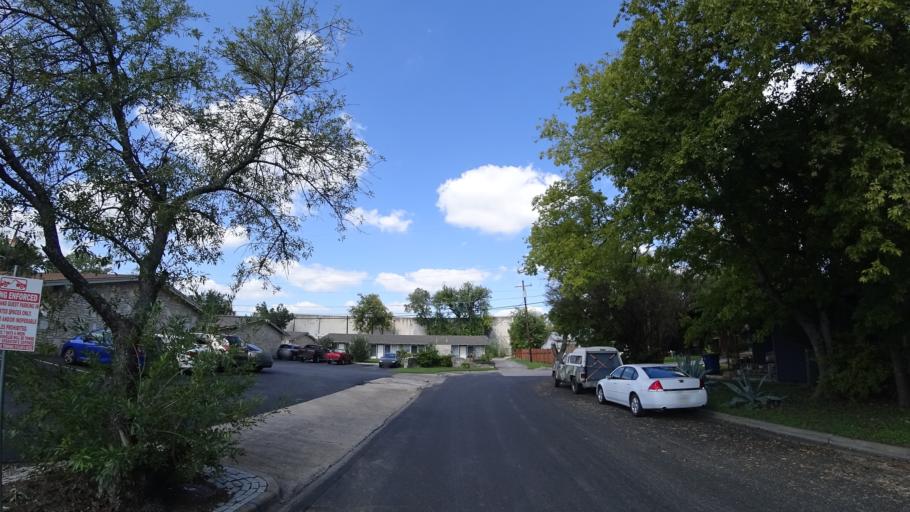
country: US
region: Texas
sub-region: Travis County
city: Austin
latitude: 30.3173
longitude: -97.7113
